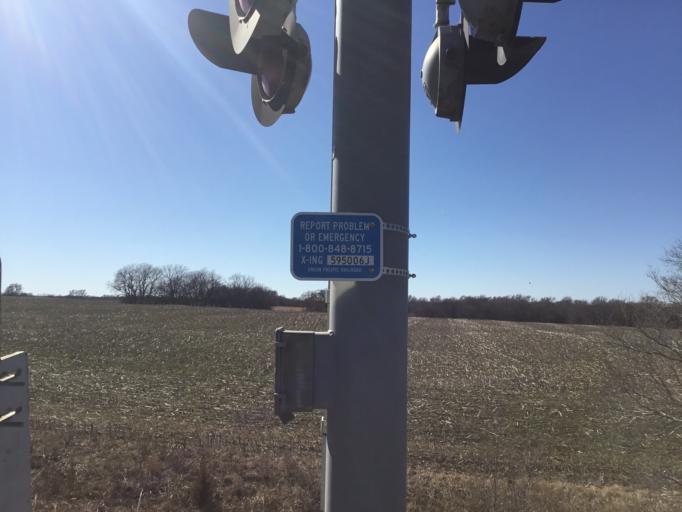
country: US
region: Kansas
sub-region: Sedgwick County
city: Kechi
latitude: 37.8892
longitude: -97.2074
